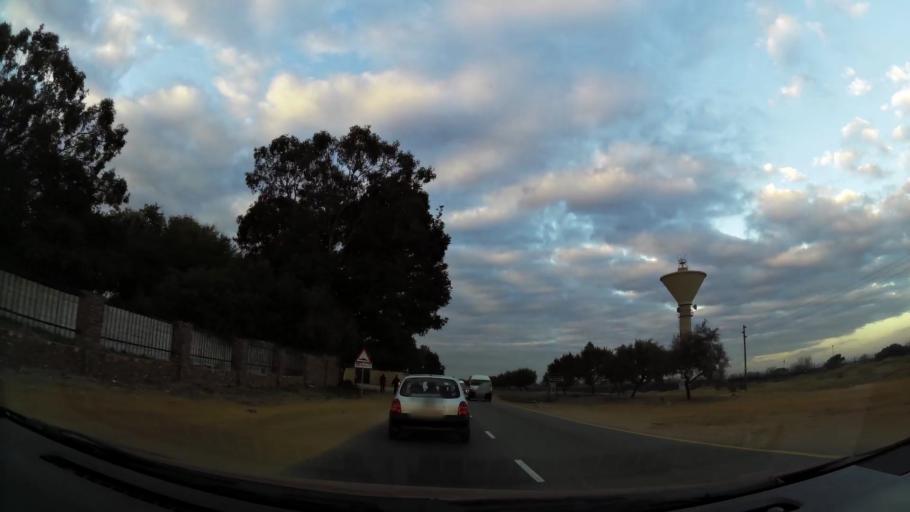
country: ZA
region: Gauteng
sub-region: City of Johannesburg Metropolitan Municipality
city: Midrand
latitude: -25.9852
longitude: 28.1582
